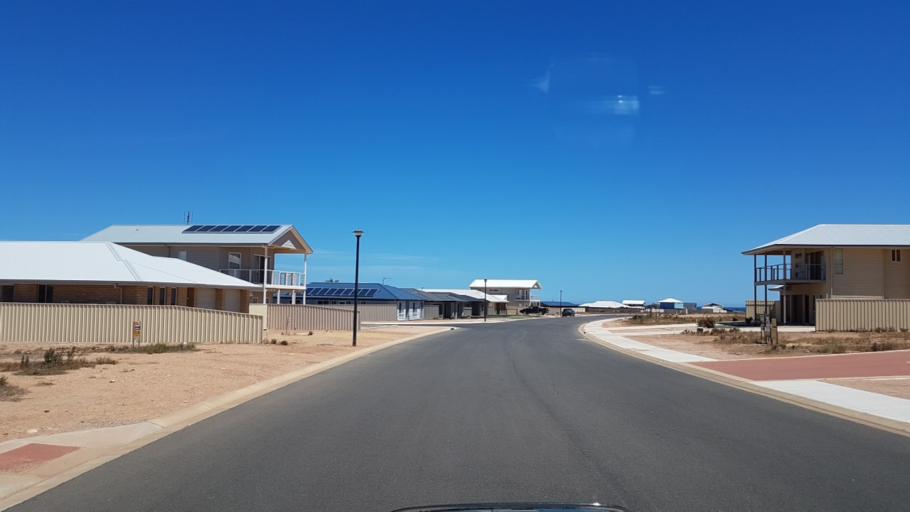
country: AU
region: South Australia
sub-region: Copper Coast
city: Wallaroo
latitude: -33.8918
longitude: 137.6326
